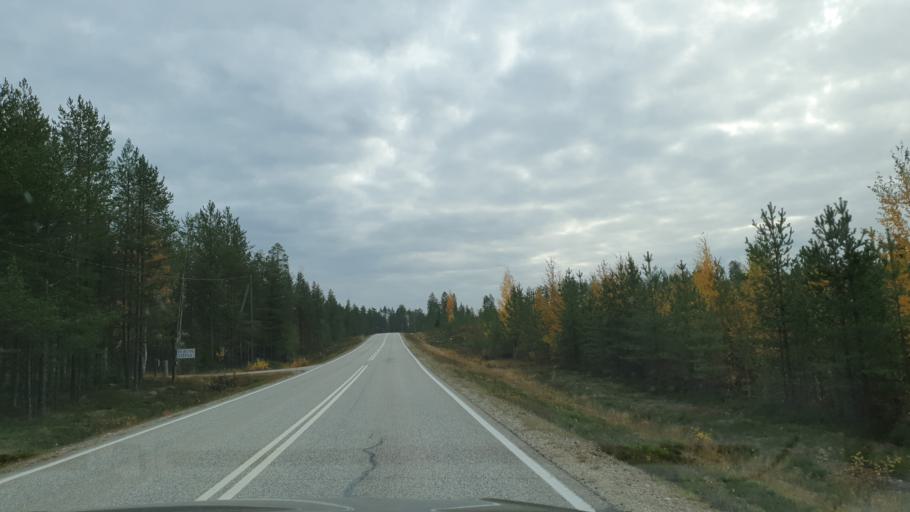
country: FI
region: Kainuu
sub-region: Kehys-Kainuu
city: Puolanka
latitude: 65.2355
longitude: 27.5909
